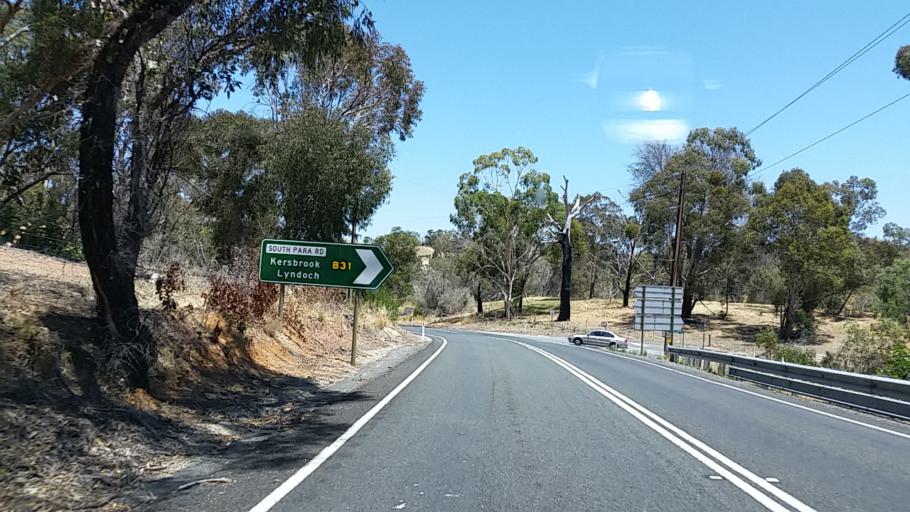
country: AU
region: South Australia
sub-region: Adelaide Hills
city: Gumeracha
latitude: -34.8218
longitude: 138.8336
